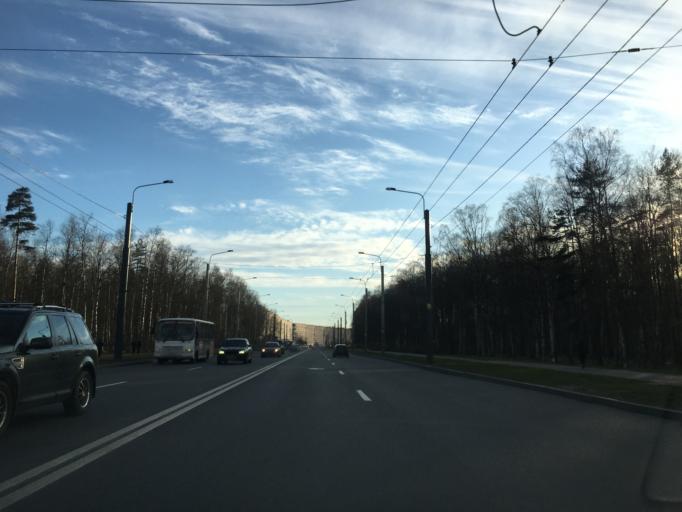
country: RU
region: St.-Petersburg
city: Dachnoye
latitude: 59.8372
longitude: 30.2299
